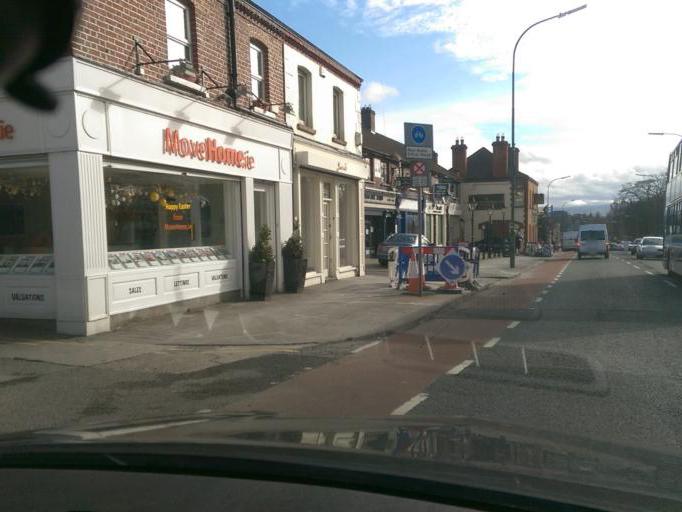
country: IE
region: Leinster
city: Drumcondra
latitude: 53.3719
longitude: -6.2530
